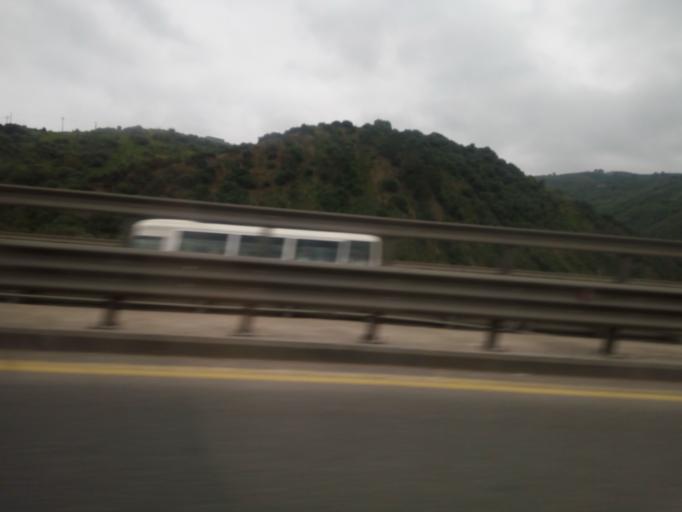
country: DZ
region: Bouira
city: Lakhdaria
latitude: 36.5532
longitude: 3.6069
